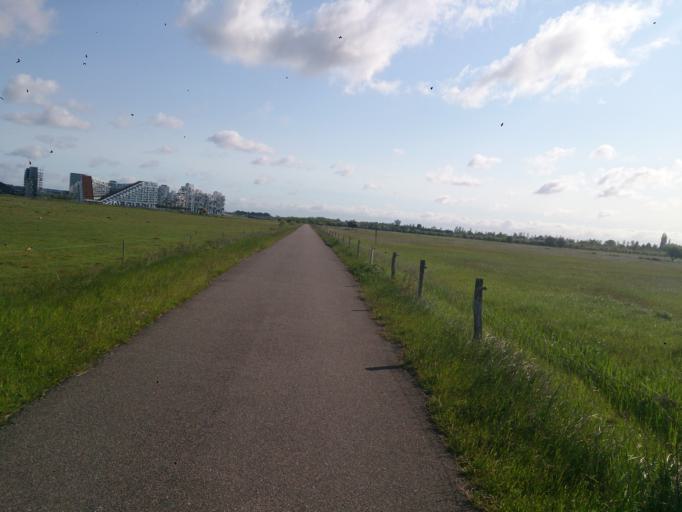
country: DK
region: Capital Region
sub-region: Tarnby Kommune
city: Tarnby
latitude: 55.6097
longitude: 12.5661
